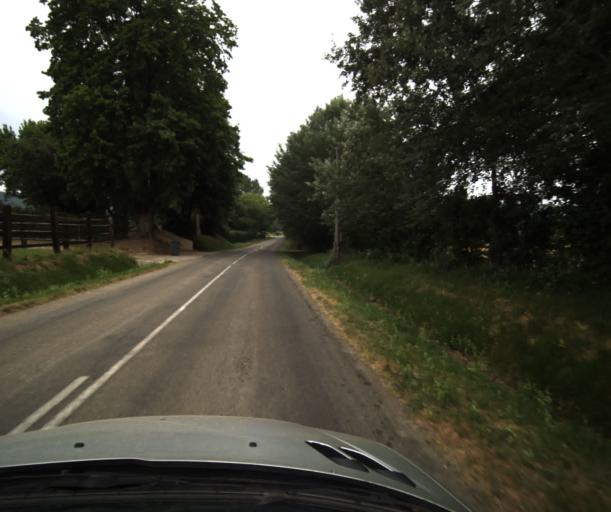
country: FR
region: Midi-Pyrenees
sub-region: Departement du Tarn-et-Garonne
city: Saint-Nicolas-de-la-Grave
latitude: 44.0830
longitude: 1.0259
